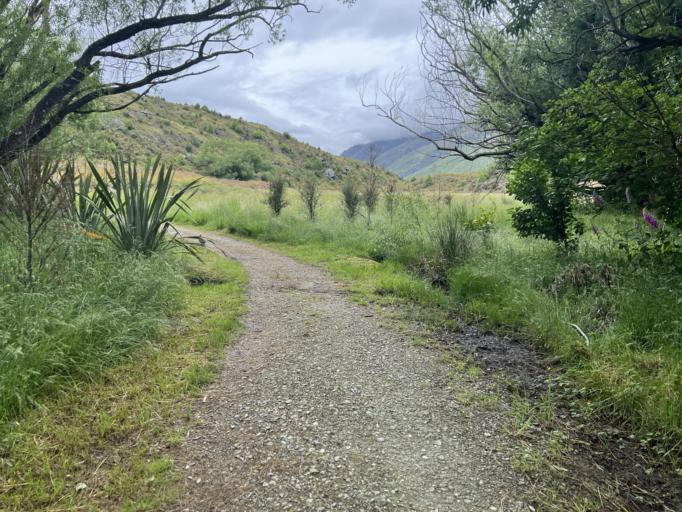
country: NZ
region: Otago
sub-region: Queenstown-Lakes District
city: Wanaka
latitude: -44.6483
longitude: 168.9624
